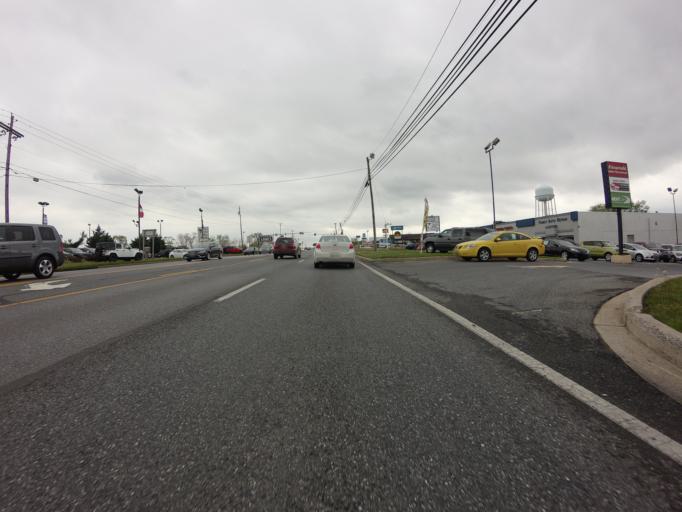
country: US
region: Maryland
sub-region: Frederick County
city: Frederick
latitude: 39.3893
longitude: -77.4095
